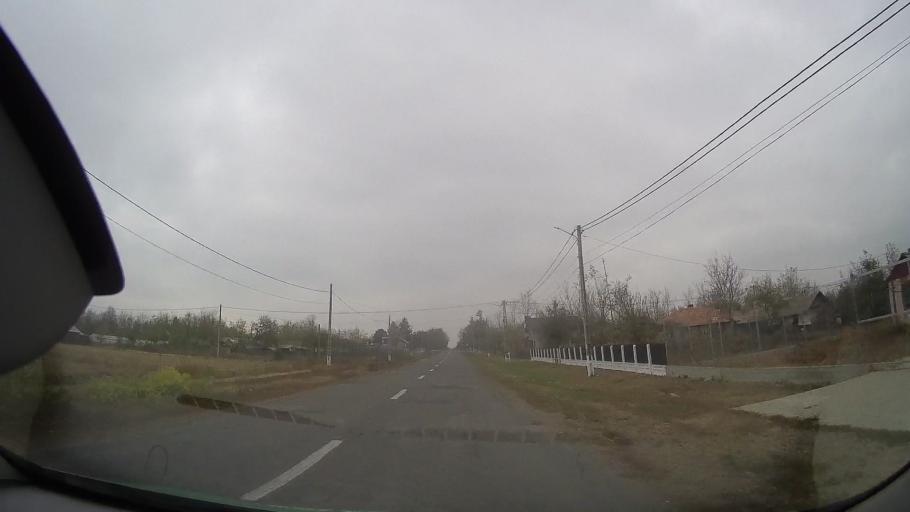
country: RO
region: Ialomita
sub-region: Comuna Valea Macrisului
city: Valea Macrisului
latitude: 44.7409
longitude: 26.8371
